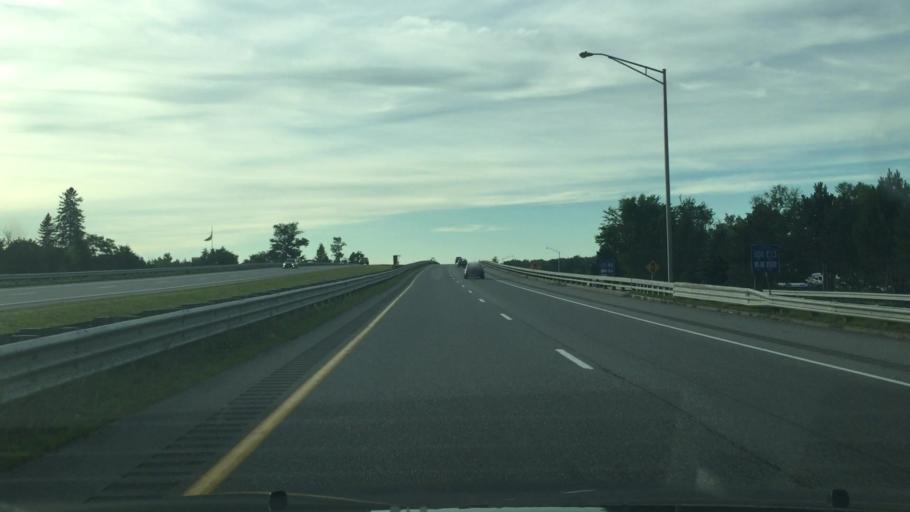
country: US
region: New Hampshire
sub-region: Merrimack County
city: Concord
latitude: 43.1901
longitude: -71.5239
